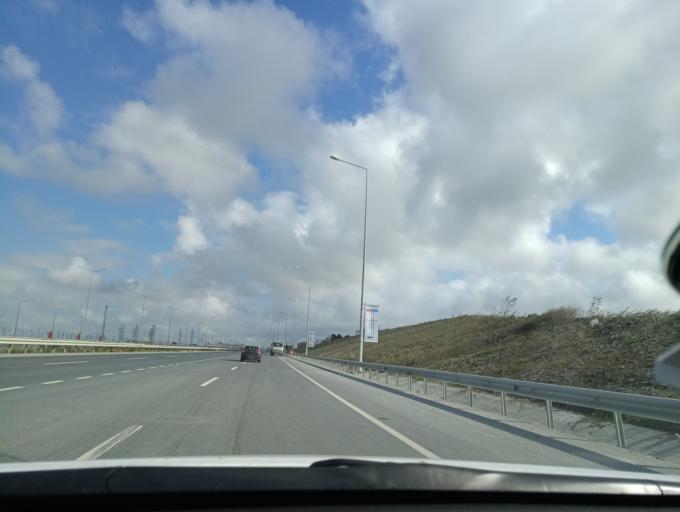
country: TR
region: Istanbul
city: Durusu
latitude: 41.2458
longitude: 28.7336
